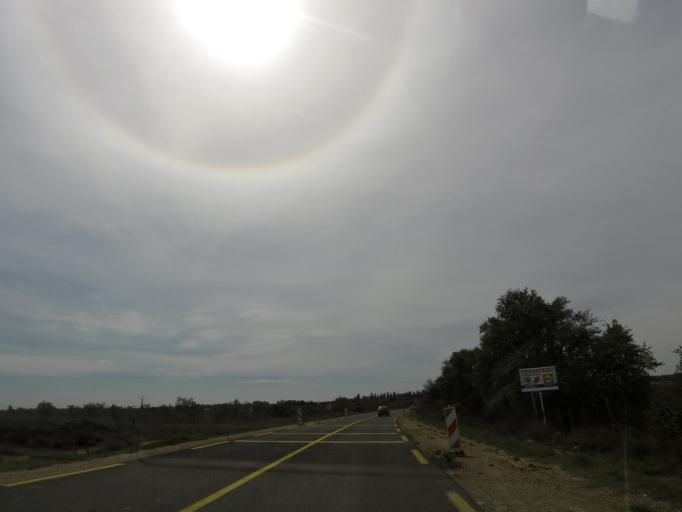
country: FR
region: Languedoc-Roussillon
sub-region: Departement de l'Herault
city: La Grande-Motte
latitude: 43.5825
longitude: 4.1039
